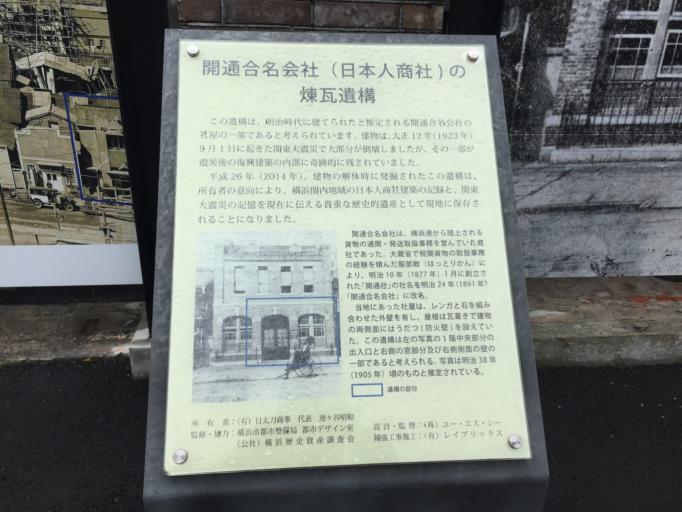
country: JP
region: Kanagawa
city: Yokohama
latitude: 35.4477
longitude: 139.6417
